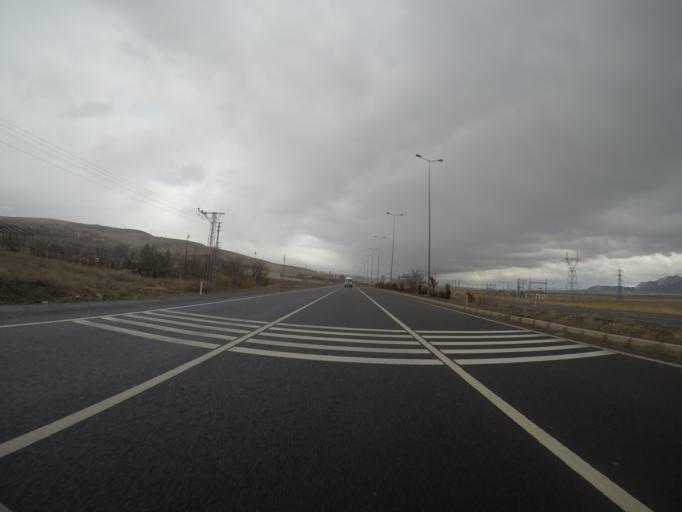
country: TR
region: Kayseri
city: Incesu
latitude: 38.7190
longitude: 35.2710
